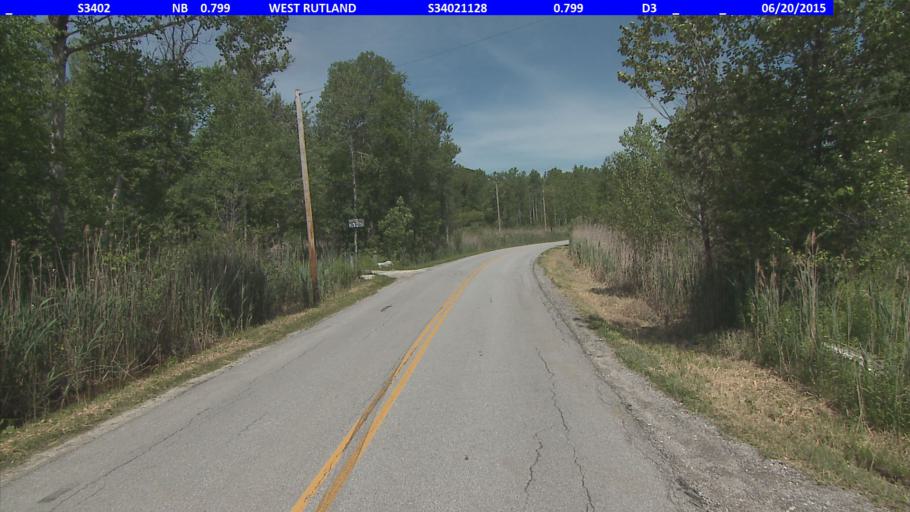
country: US
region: Vermont
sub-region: Rutland County
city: West Rutland
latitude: 43.6051
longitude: -73.0540
